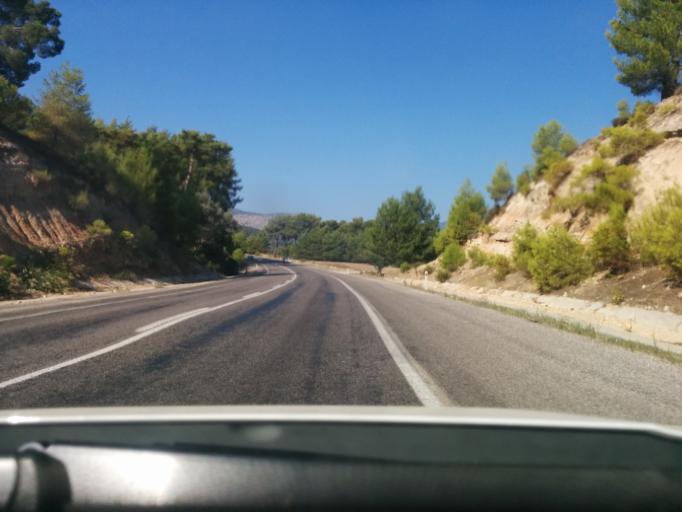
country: TR
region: Mugla
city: Esen
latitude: 36.4053
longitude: 29.2952
